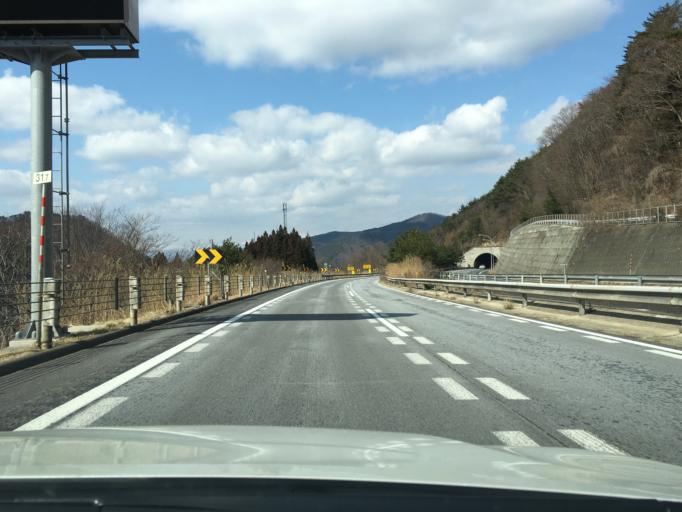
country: JP
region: Yamagata
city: Yamagata-shi
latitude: 38.2282
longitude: 140.4111
